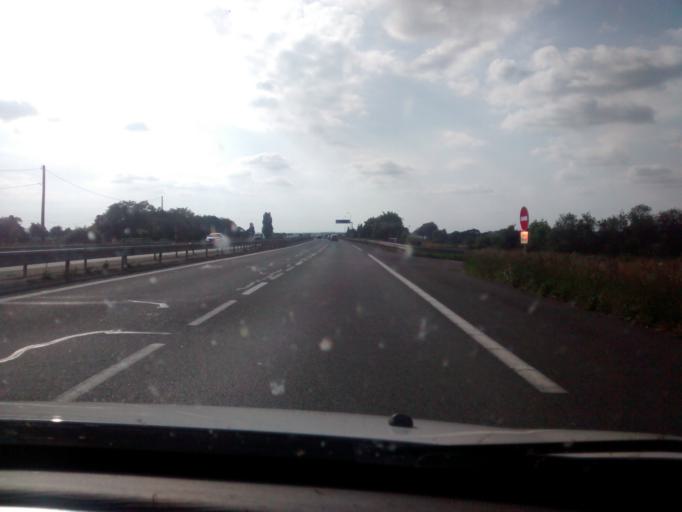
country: FR
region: Pays de la Loire
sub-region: Departement de la Mayenne
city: Bonchamp-les-Laval
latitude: 48.0941
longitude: -0.6880
